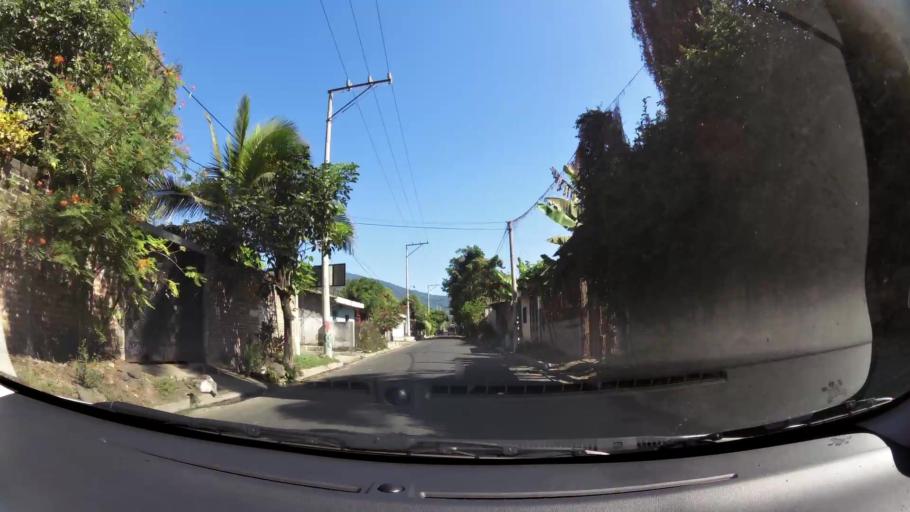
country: SV
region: La Libertad
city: Santa Tecla
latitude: 13.7312
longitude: -89.3705
